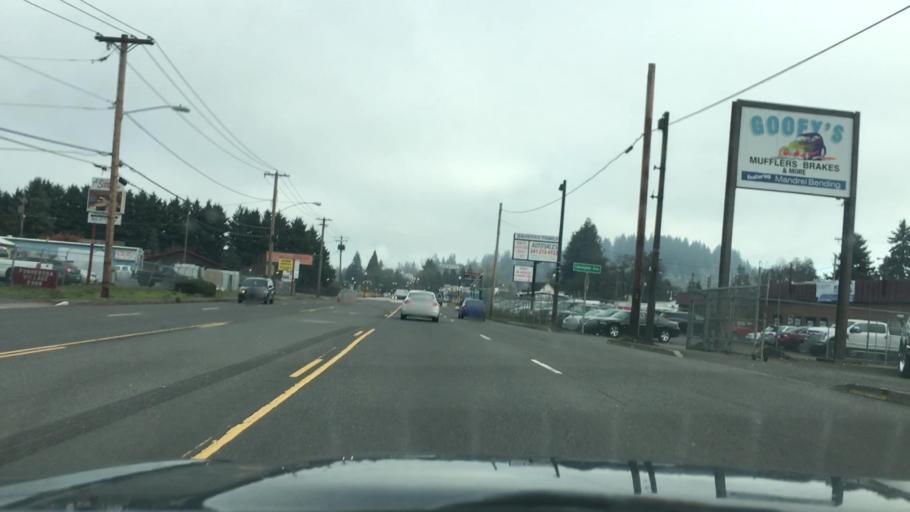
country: US
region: Oregon
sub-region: Lane County
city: Springfield
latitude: 44.0448
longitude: -123.0364
